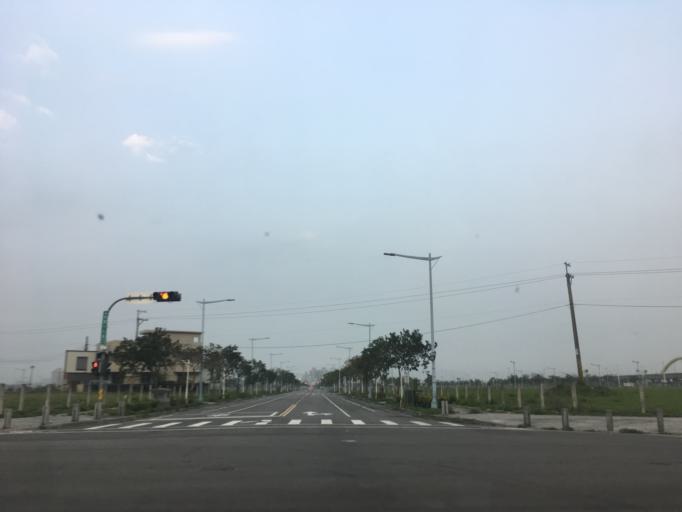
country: TW
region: Taiwan
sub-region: Taichung City
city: Taichung
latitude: 24.1979
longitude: 120.6750
